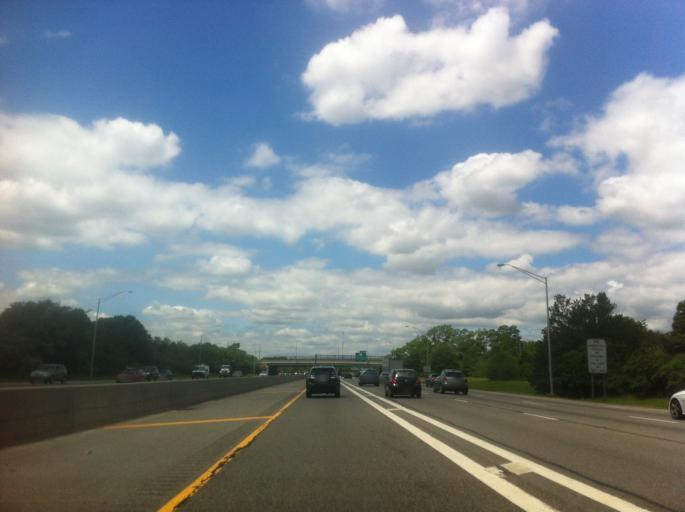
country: US
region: New York
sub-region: Suffolk County
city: Islandia
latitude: 40.8098
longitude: -73.1557
